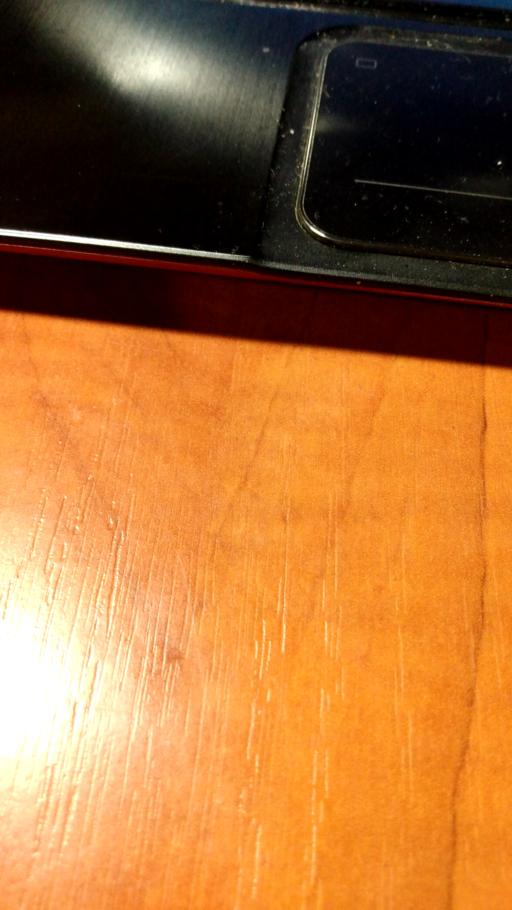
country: RU
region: Novgorod
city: Marevo
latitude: 57.3322
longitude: 32.0261
